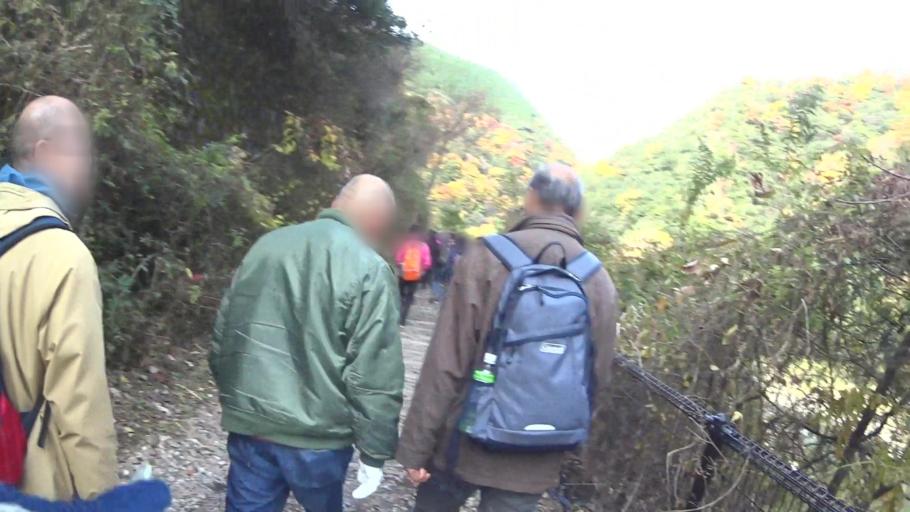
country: JP
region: Hyogo
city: Takarazuka
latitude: 34.8354
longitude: 135.3227
